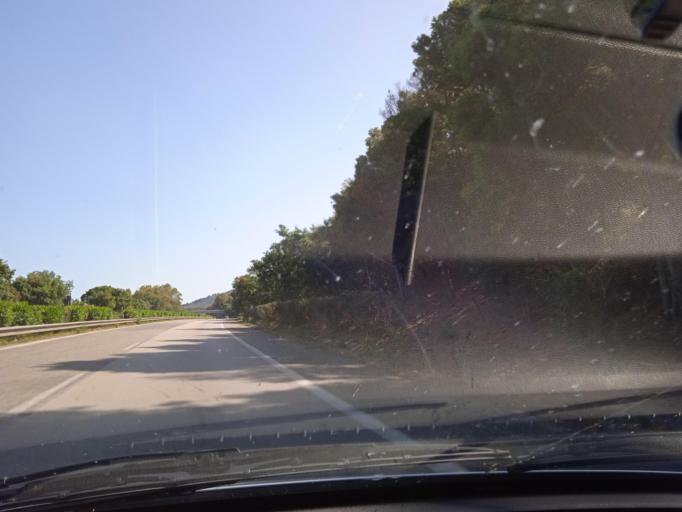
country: IT
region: Sicily
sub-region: Messina
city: Capo d'Orlando
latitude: 38.1225
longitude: 14.7281
